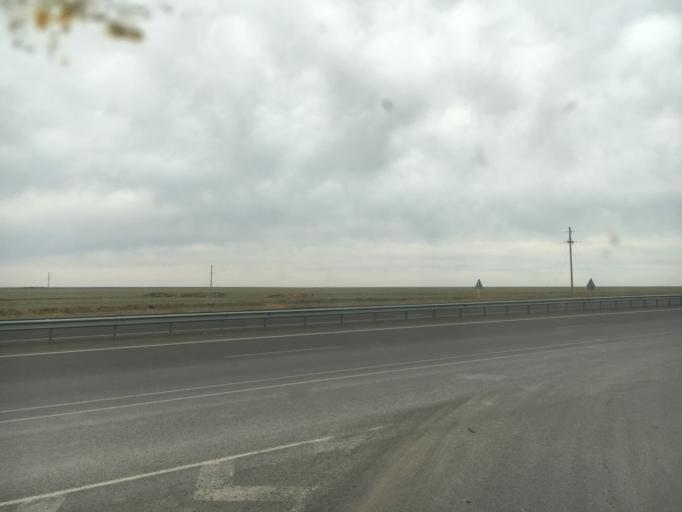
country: KZ
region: Qyzylorda
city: Shalqiya
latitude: 43.6066
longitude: 67.6710
